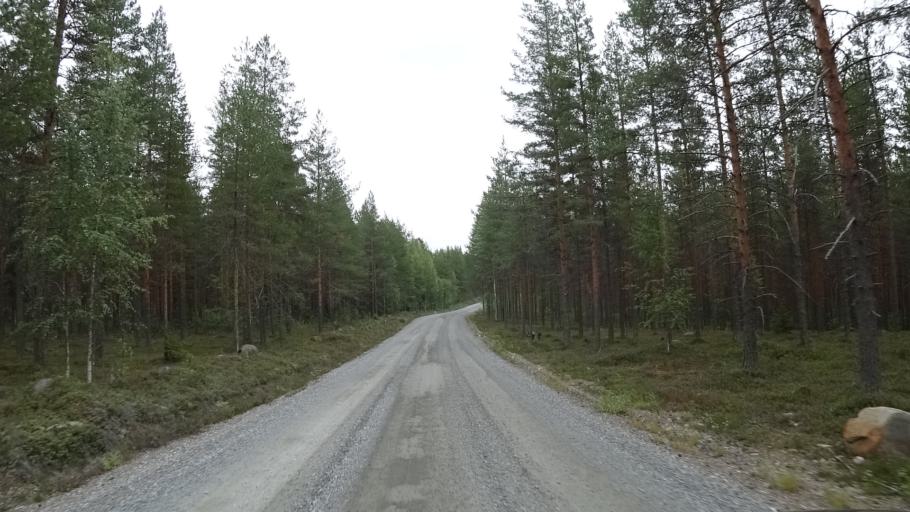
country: FI
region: North Karelia
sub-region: Pielisen Karjala
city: Lieksa
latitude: 63.3731
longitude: 30.3726
